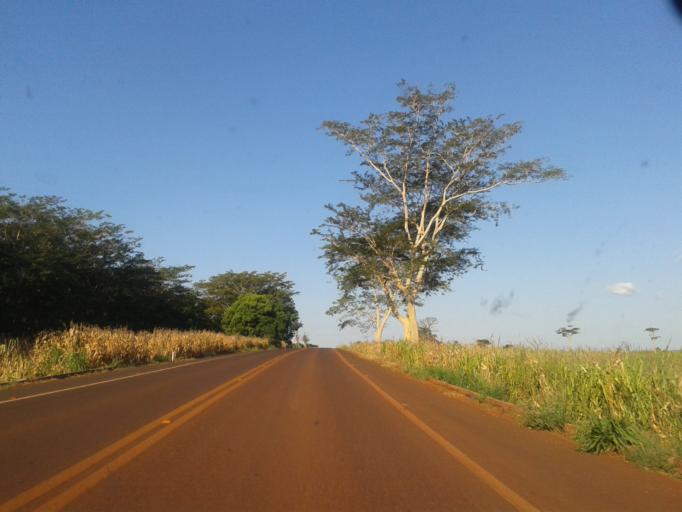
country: BR
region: Minas Gerais
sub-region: Santa Vitoria
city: Santa Vitoria
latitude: -18.6913
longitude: -49.9018
